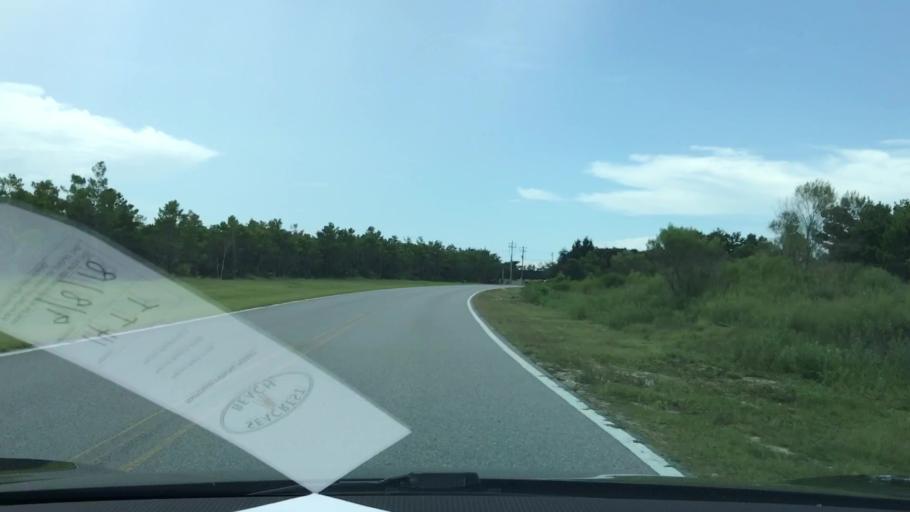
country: US
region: Florida
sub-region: Walton County
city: Seaside
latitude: 30.2896
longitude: -86.0368
